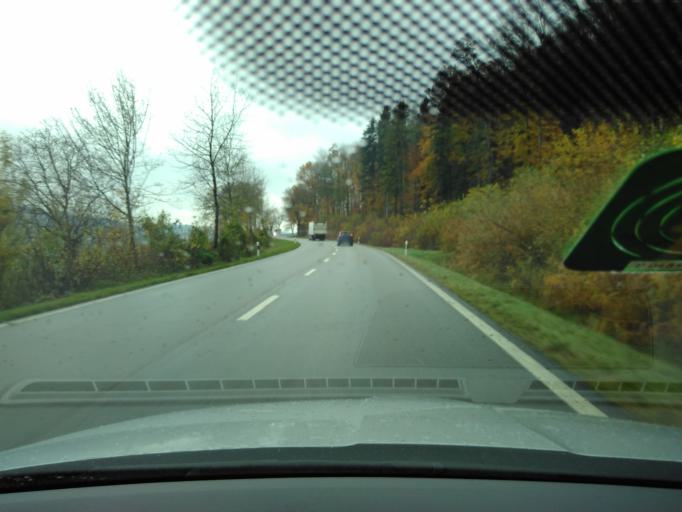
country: CH
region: Aargau
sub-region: Bezirk Zofingen
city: Kirchleerau
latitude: 47.2586
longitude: 8.0652
